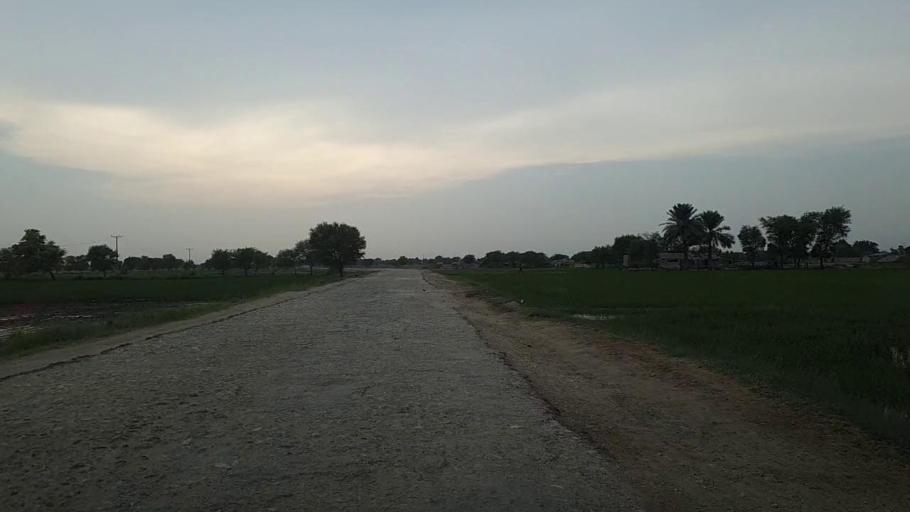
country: PK
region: Sindh
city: Khanpur
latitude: 27.8485
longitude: 69.4447
